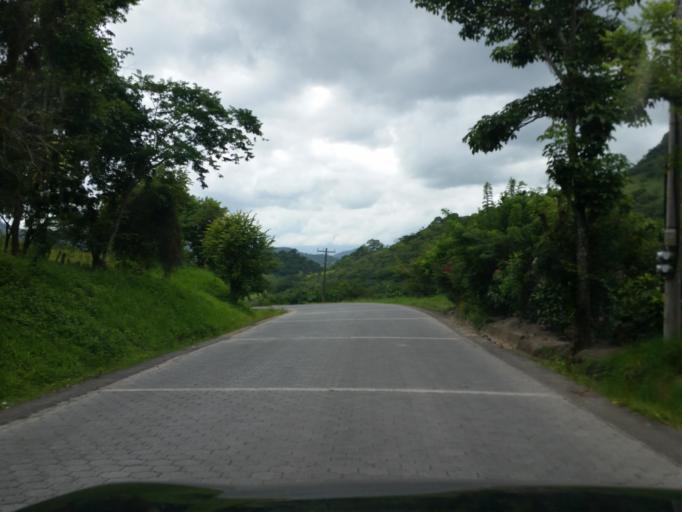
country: NI
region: Matagalpa
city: San Ramon
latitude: 12.9333
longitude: -85.8547
